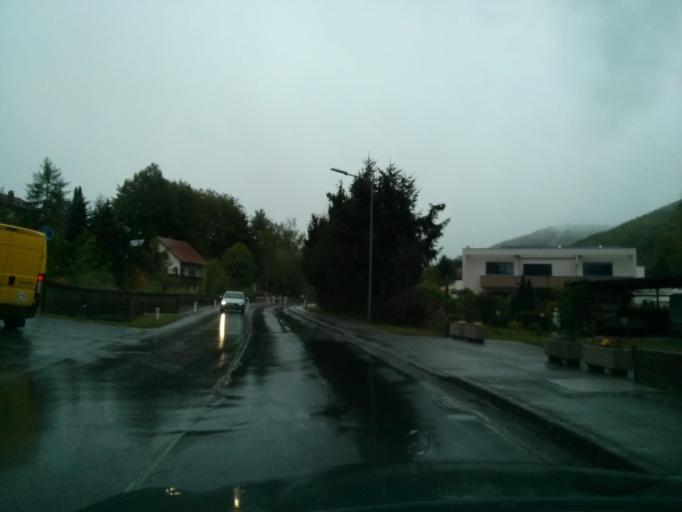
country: AT
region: Styria
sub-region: Politischer Bezirk Graz-Umgebung
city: Stattegg
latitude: 47.1312
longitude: 15.4243
